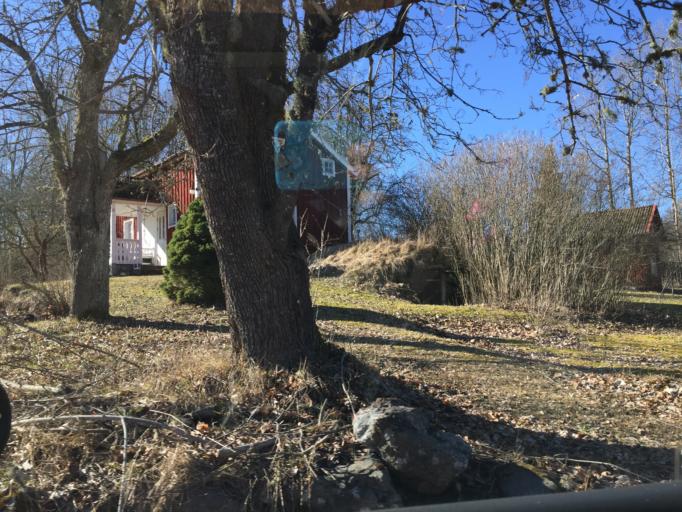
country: SE
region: Soedermanland
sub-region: Vingakers Kommun
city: Vingaker
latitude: 59.0738
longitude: 15.8306
